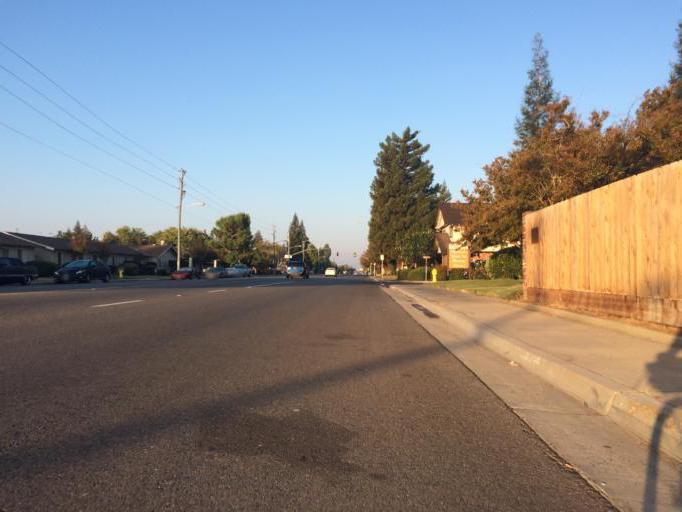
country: US
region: California
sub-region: Fresno County
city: Tarpey Village
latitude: 36.8013
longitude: -119.7253
